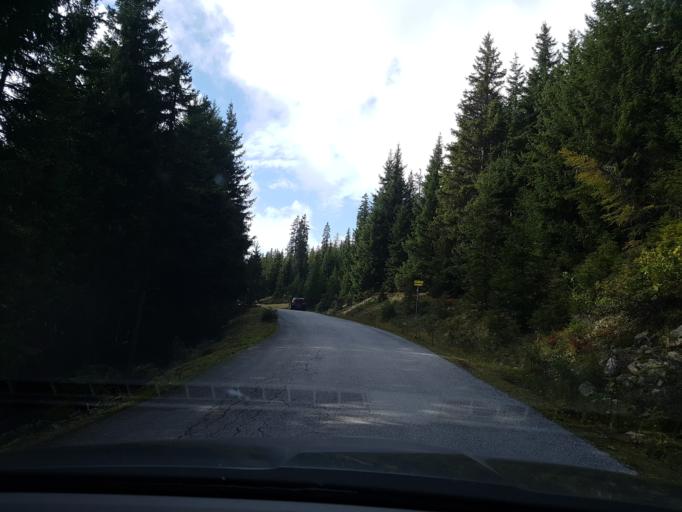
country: AT
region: Salzburg
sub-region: Politischer Bezirk Sankt Johann im Pongau
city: Radstadt
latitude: 47.4067
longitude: 13.4778
